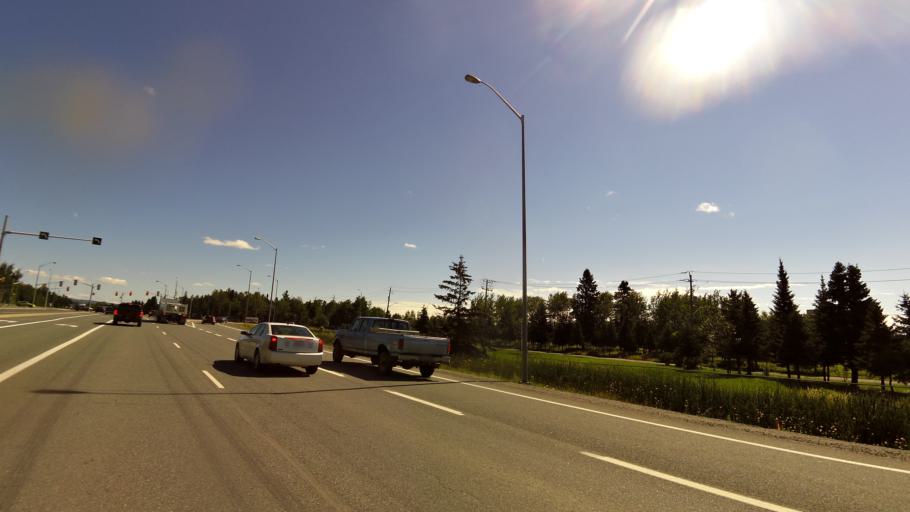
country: CA
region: Ontario
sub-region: Thunder Bay District
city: Thunder Bay
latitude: 48.4488
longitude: -89.2527
